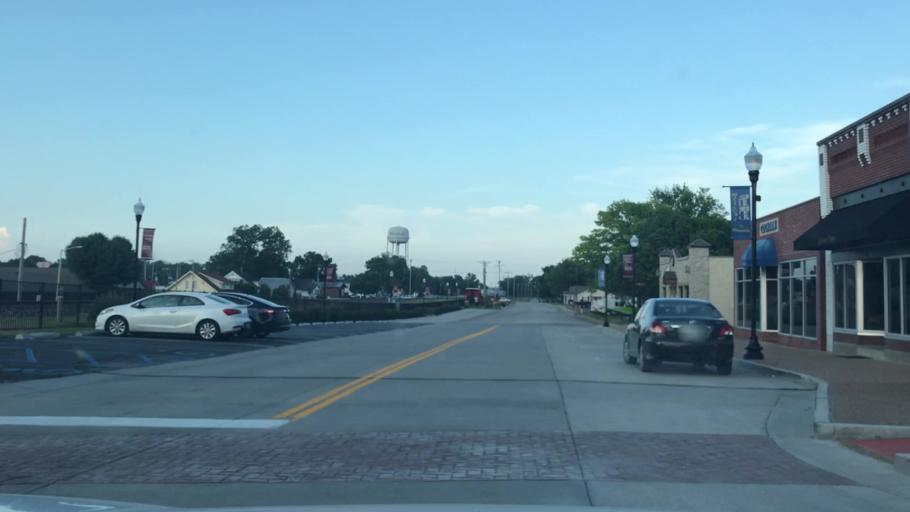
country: US
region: Missouri
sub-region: Saint Charles County
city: Wentzville
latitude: 38.8110
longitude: -90.8529
